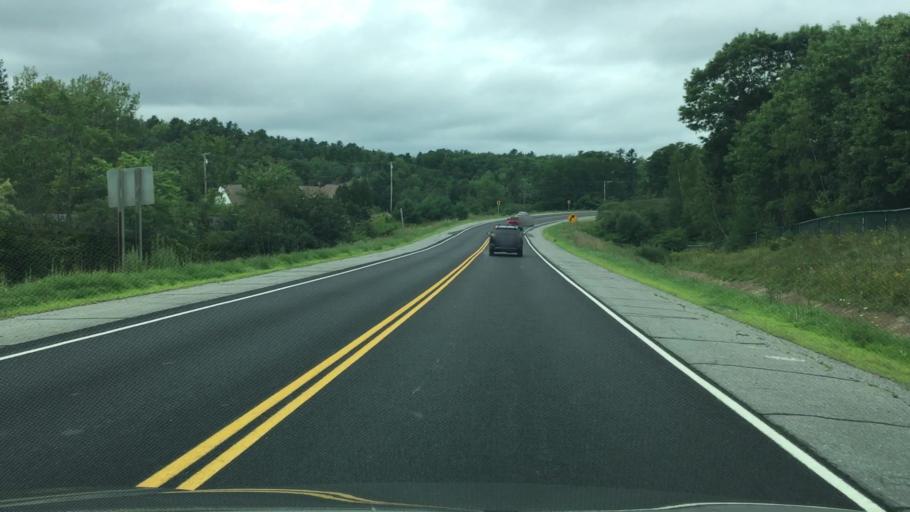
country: US
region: Maine
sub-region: Penobscot County
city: Orrington
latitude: 44.6965
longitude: -68.8172
